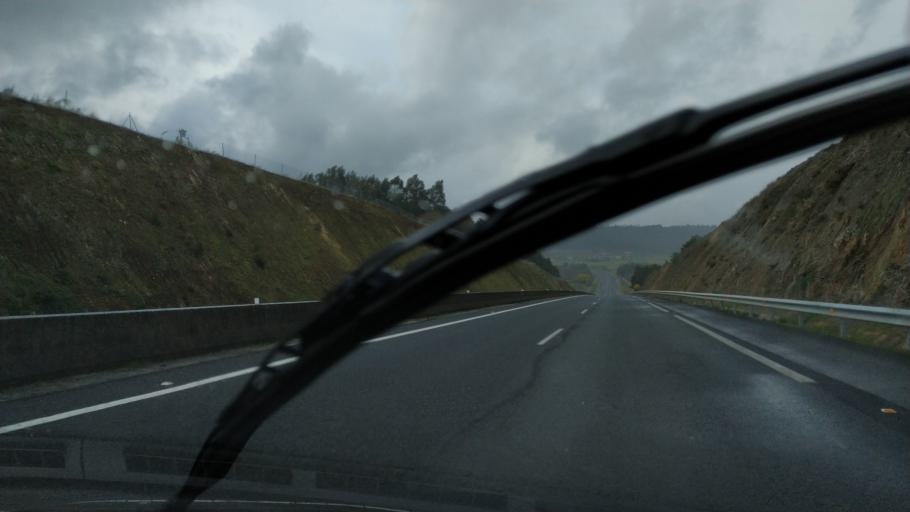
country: ES
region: Galicia
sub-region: Provincia de Pontevedra
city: Silleda
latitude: 42.7214
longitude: -8.3124
